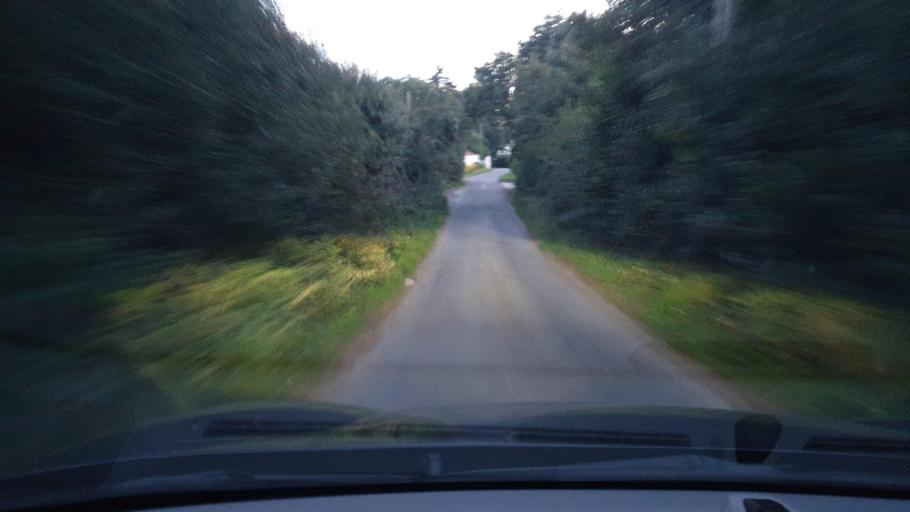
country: IE
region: Leinster
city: Lusk
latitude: 53.5311
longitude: -6.1379
